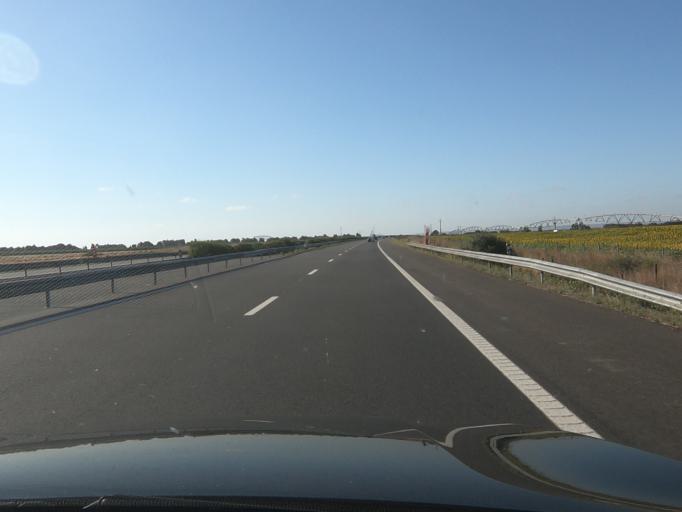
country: PT
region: Beja
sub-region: Aljustrel
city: Aljustrel
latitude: 37.9854
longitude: -8.2625
